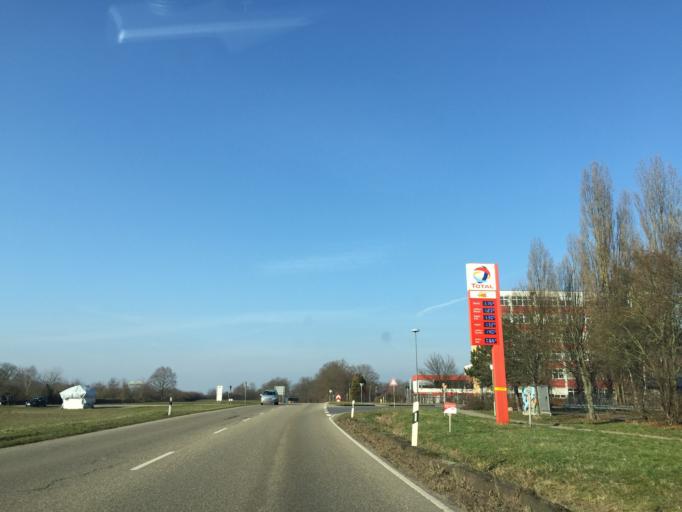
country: DE
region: Baden-Wuerttemberg
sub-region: Karlsruhe Region
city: Eppelheim
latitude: 49.4232
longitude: 8.6382
